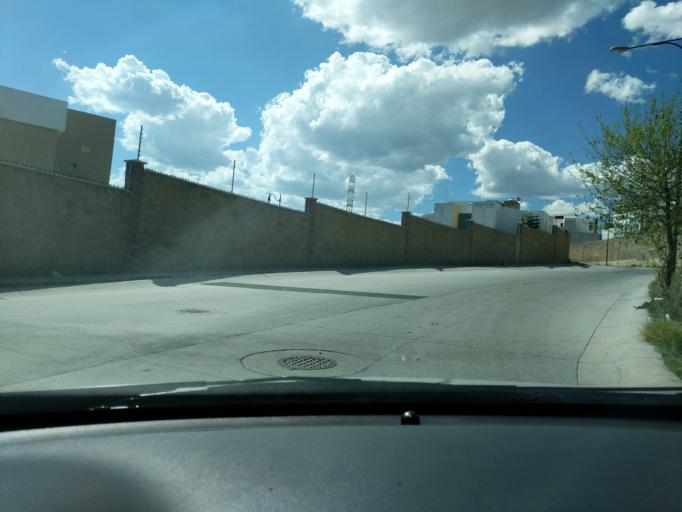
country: MX
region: Guanajuato
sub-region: Leon
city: Medina
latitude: 21.1349
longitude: -101.6036
